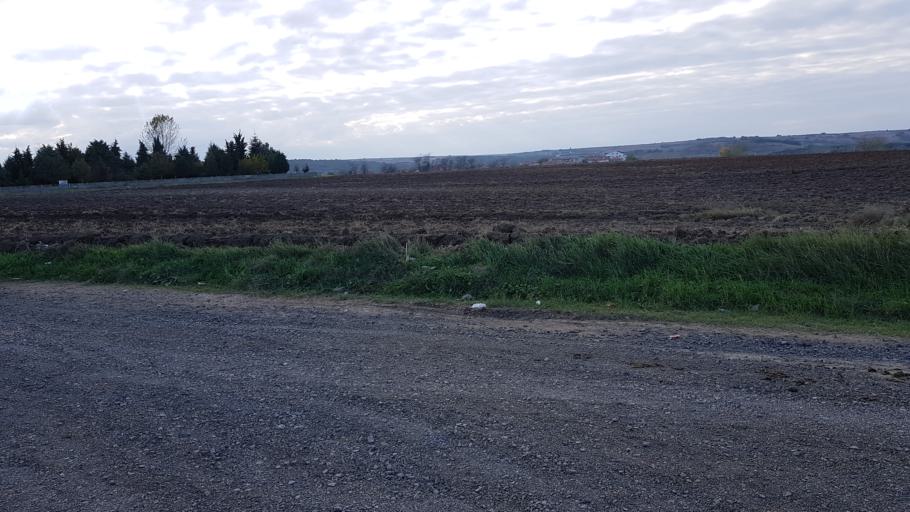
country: TR
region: Tekirdag
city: Muratli
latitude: 41.1812
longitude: 27.4965
